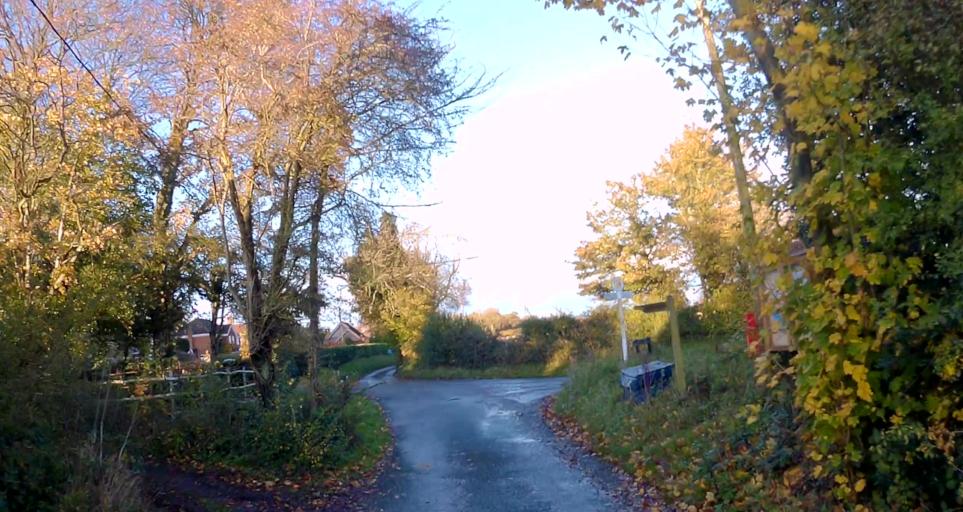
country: GB
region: England
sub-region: Hampshire
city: Basingstoke
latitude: 51.2047
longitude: -1.0801
